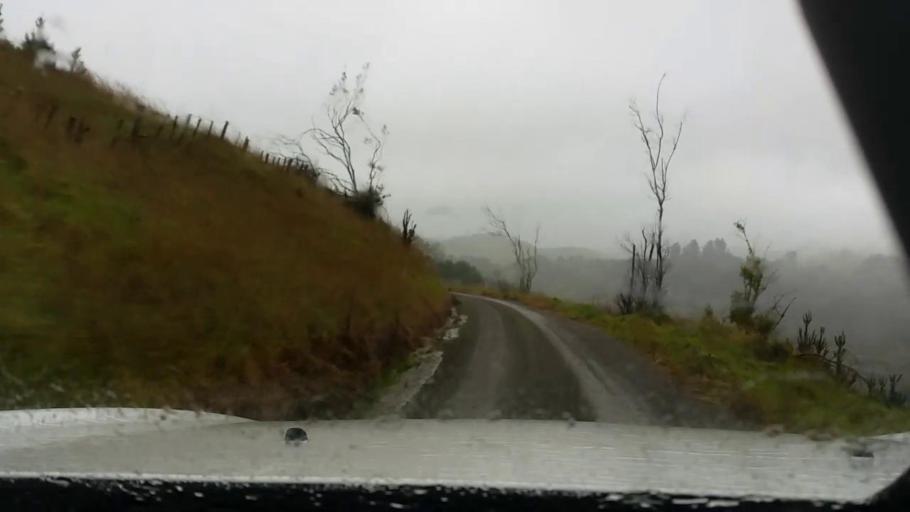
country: NZ
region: Wellington
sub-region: Masterton District
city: Masterton
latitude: -41.1991
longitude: 175.8114
